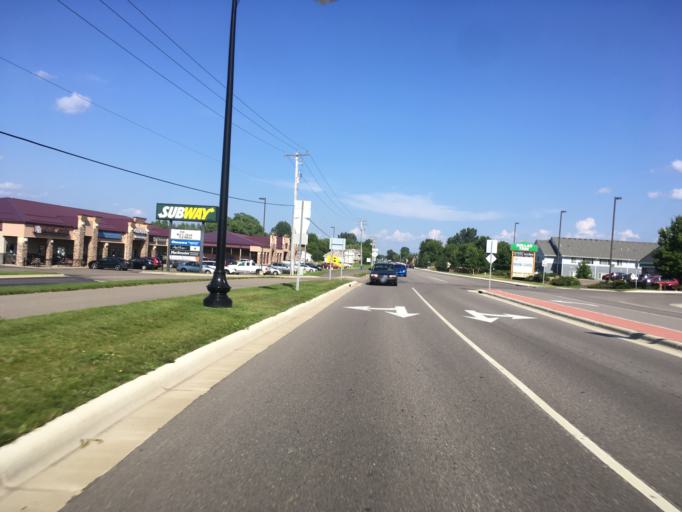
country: US
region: Minnesota
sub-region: Stearns County
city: Sartell
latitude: 45.6155
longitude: -94.2264
